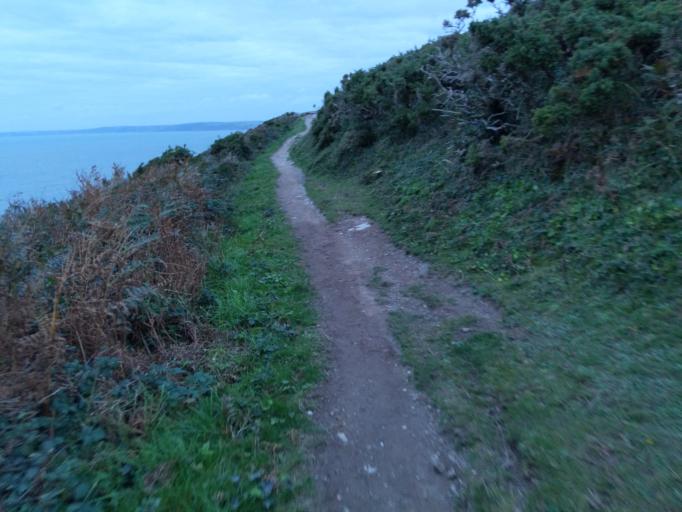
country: GB
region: England
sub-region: Cornwall
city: Millbrook
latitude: 50.3184
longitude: -4.2234
